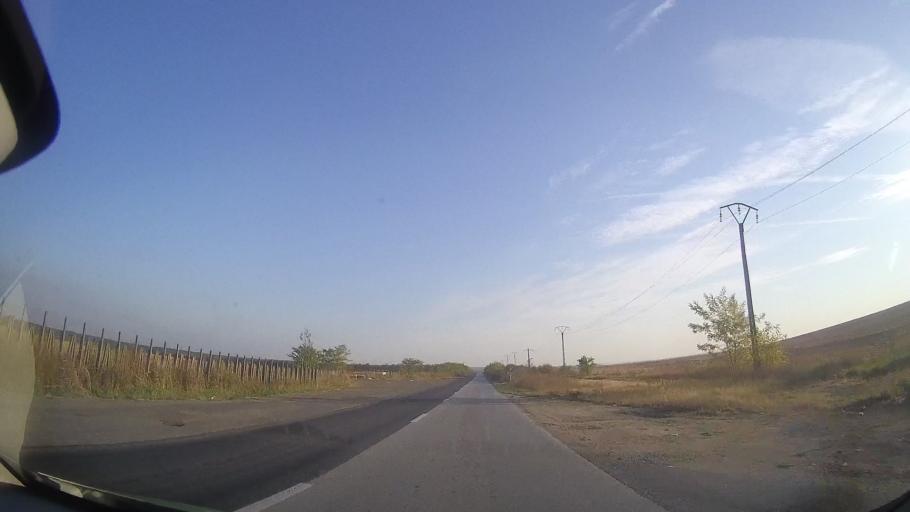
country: RO
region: Timis
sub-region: Comuna Giarmata
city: Giarmata
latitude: 45.8652
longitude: 21.3184
